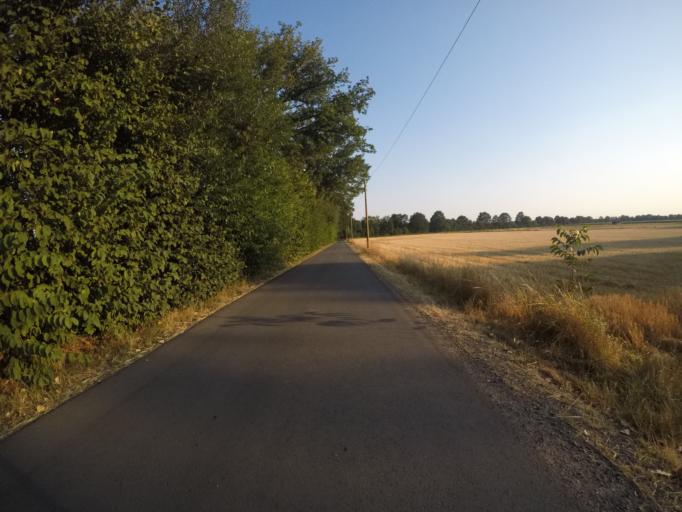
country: DE
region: North Rhine-Westphalia
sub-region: Regierungsbezirk Munster
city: Isselburg
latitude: 51.8526
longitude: 6.5153
